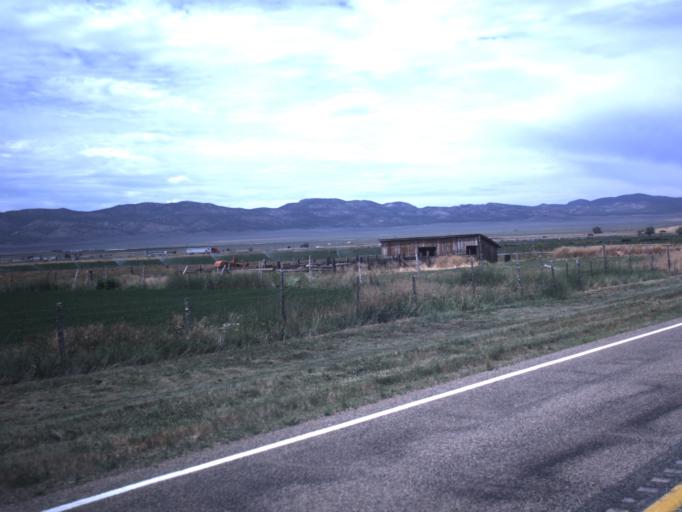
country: US
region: Utah
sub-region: Iron County
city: Parowan
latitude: 37.9016
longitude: -112.7749
